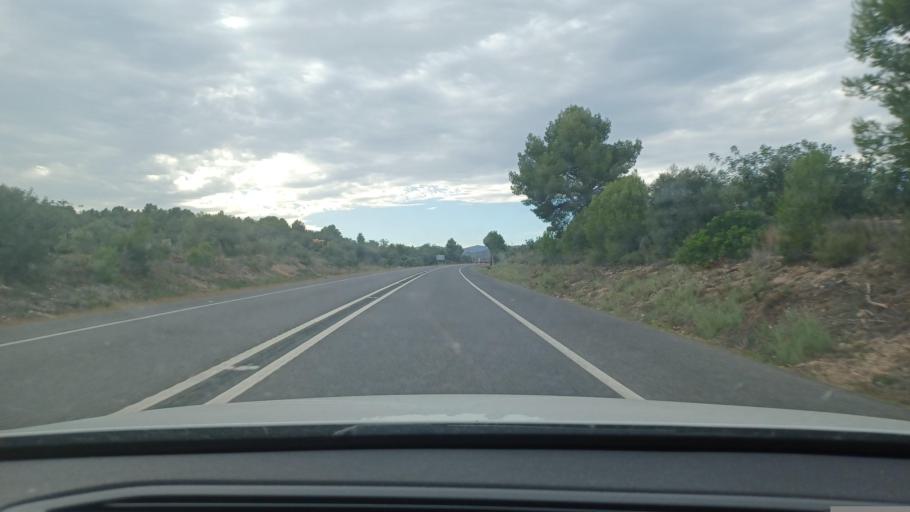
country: ES
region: Catalonia
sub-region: Provincia de Tarragona
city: l'Ametlla de Mar
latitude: 40.8952
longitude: 0.7583
